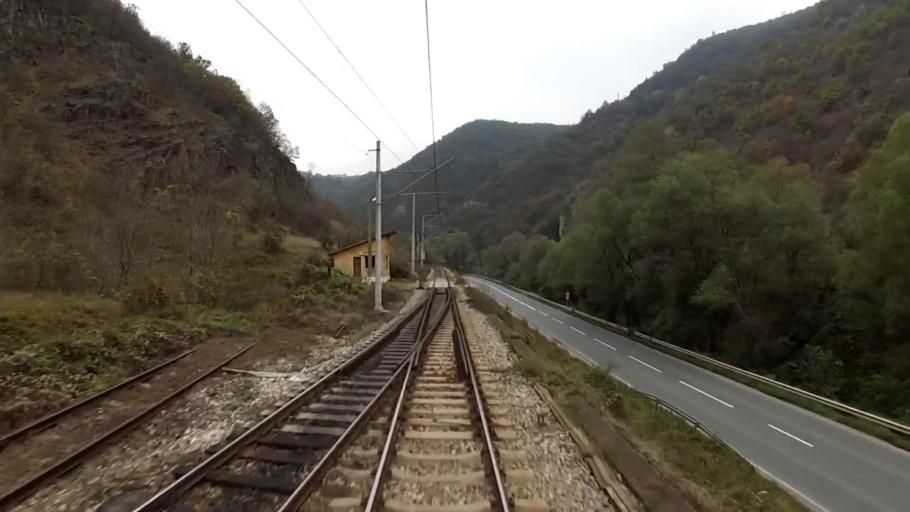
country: RS
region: Central Serbia
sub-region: Pirotski Okrug
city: Dimitrovgrad
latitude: 42.9737
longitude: 22.8501
